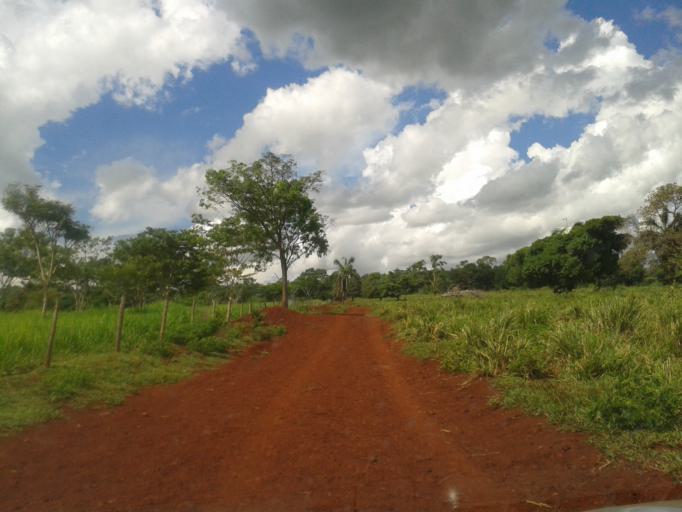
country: BR
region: Minas Gerais
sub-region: Capinopolis
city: Capinopolis
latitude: -18.7692
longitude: -49.8282
